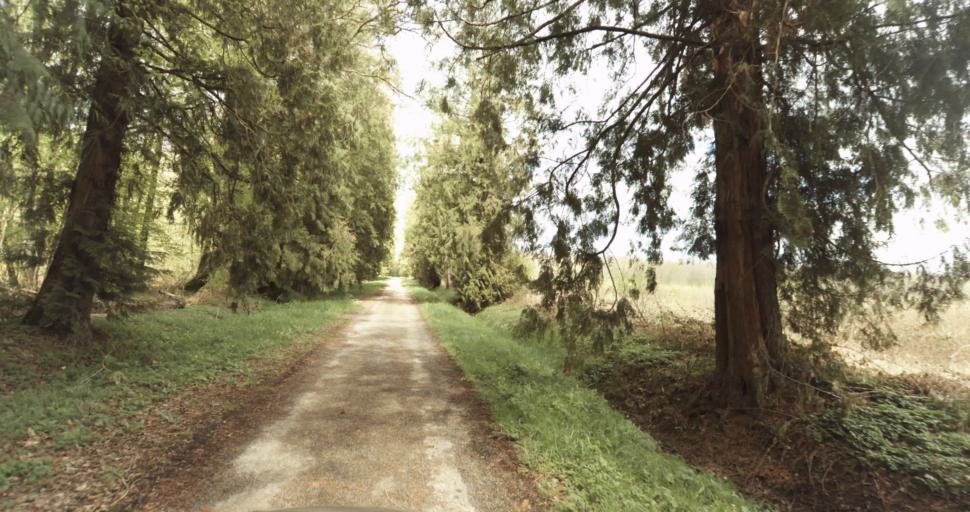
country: FR
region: Bourgogne
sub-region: Departement de la Cote-d'Or
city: Auxonne
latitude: 47.1627
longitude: 5.4231
